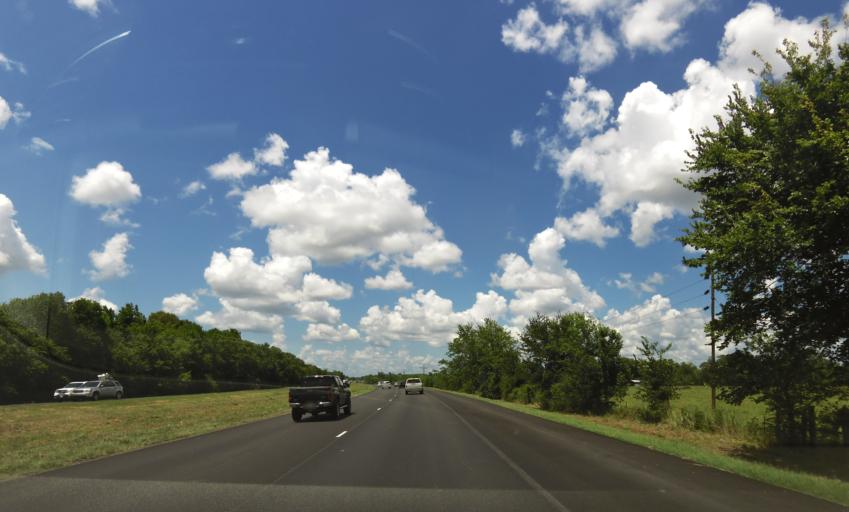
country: US
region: Texas
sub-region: San Jacinto County
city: Shepherd
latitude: 30.5783
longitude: -94.9455
